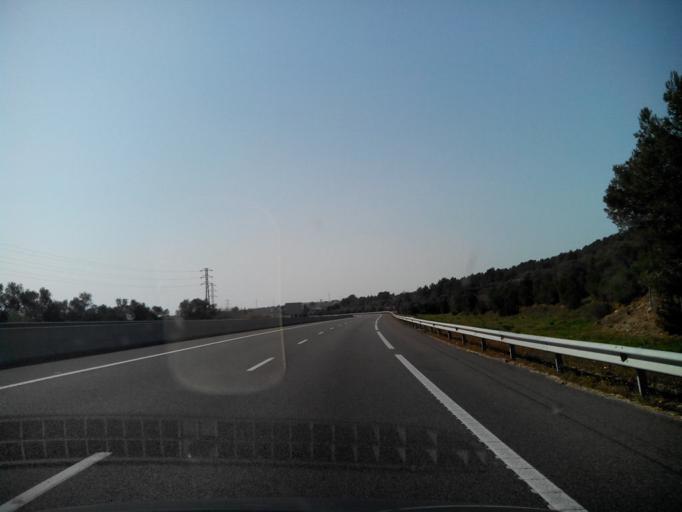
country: ES
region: Catalonia
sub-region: Provincia de Tarragona
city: Alcover
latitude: 41.2462
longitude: 1.1709
